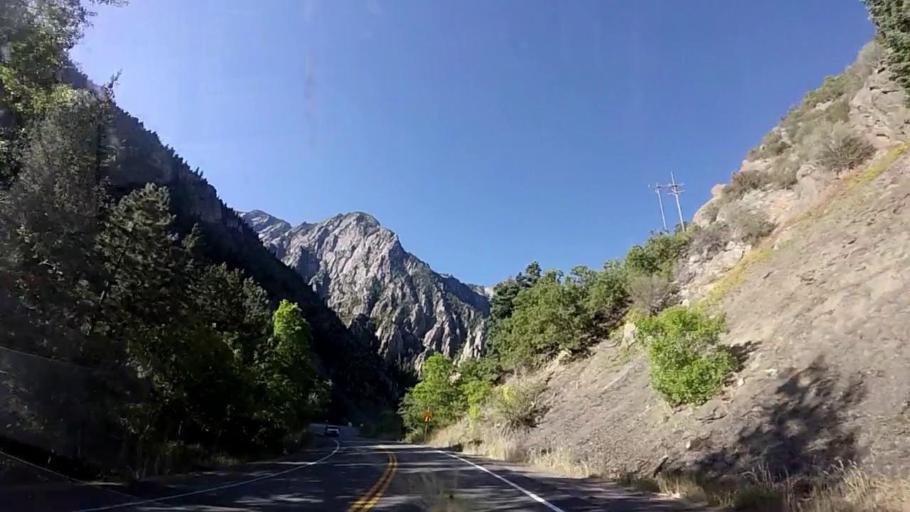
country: US
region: Utah
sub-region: Salt Lake County
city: Cottonwood Heights
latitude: 40.6277
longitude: -111.7420
